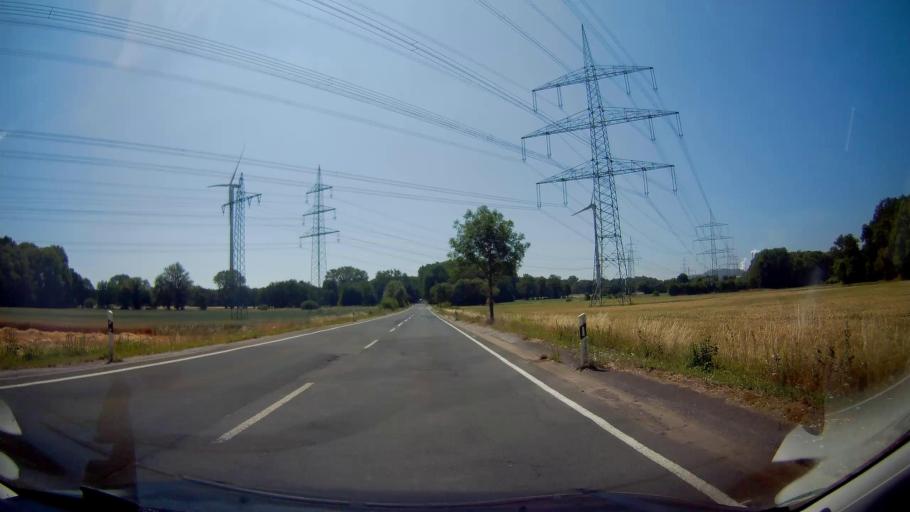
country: DE
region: North Rhine-Westphalia
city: Marl
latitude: 51.6461
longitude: 7.0441
